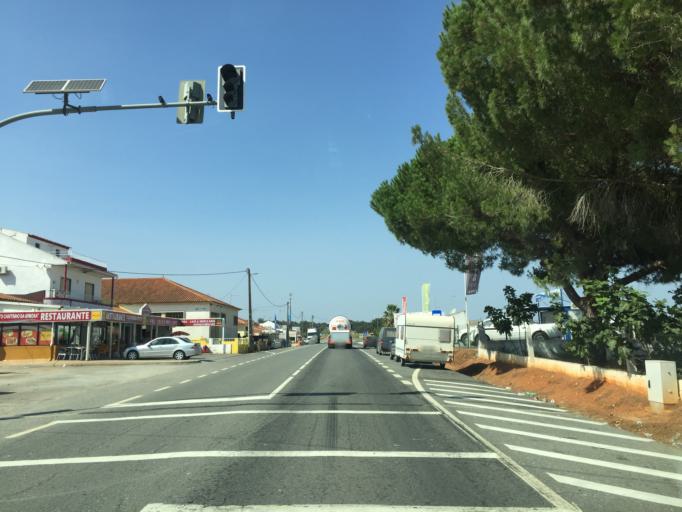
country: PT
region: Beja
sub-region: Aljustrel
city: Aljustrel
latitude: 37.9469
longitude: -8.3807
